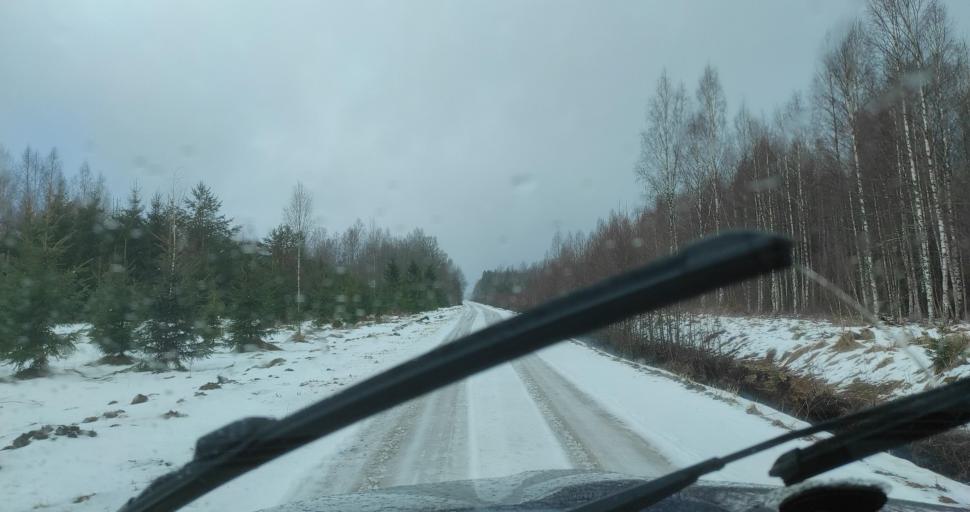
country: LV
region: Dundaga
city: Dundaga
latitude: 57.3874
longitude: 22.1398
